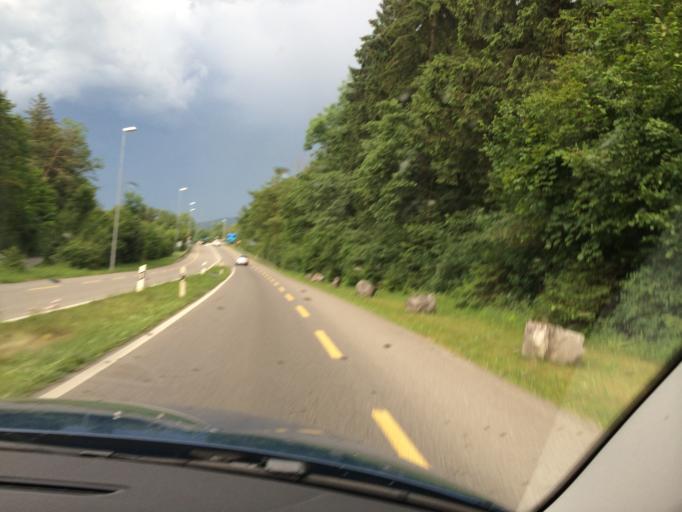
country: CH
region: Bern
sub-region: Bern-Mittelland District
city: Rubigen
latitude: 46.8888
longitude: 7.5332
